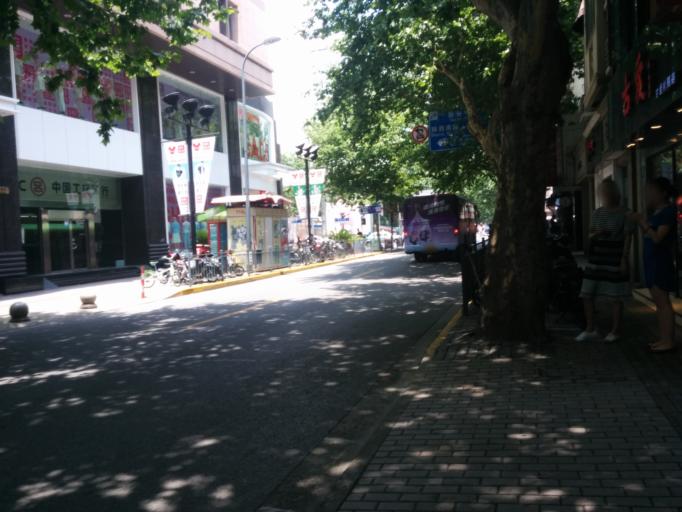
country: CN
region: Shanghai Shi
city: Shanghai
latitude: 31.2190
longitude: 121.4569
